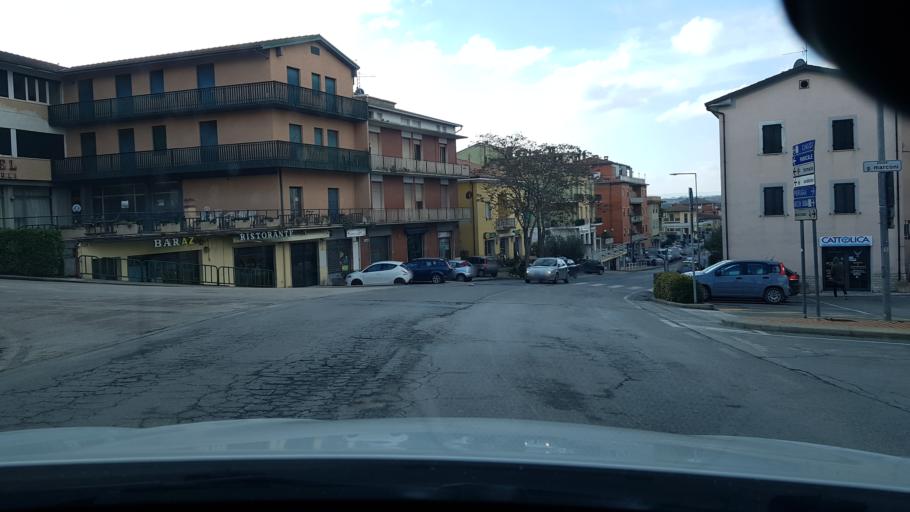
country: IT
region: Umbria
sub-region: Provincia di Perugia
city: Castiglione del Lago
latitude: 43.1265
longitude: 12.0480
